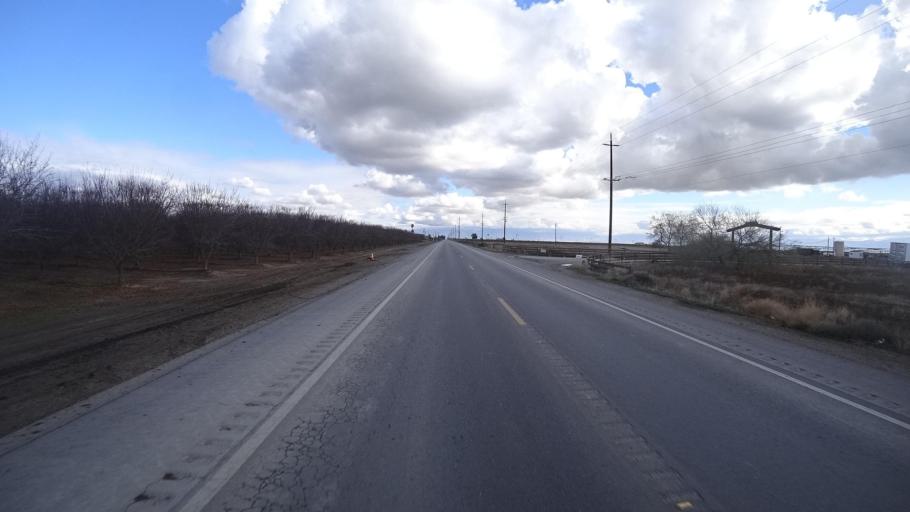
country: US
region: California
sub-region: Kern County
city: Greenfield
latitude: 35.2089
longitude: -119.0956
